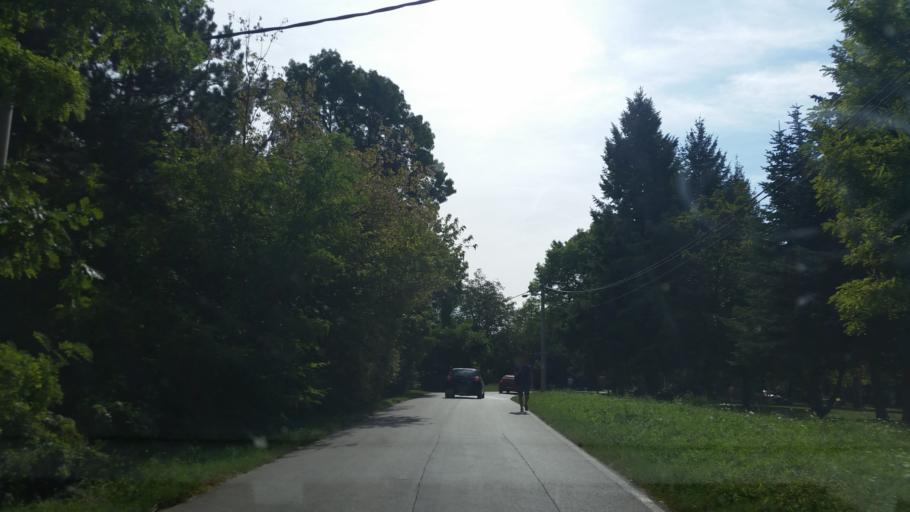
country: RS
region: Central Serbia
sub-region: Belgrade
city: Palilula
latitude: 44.8059
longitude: 20.5103
